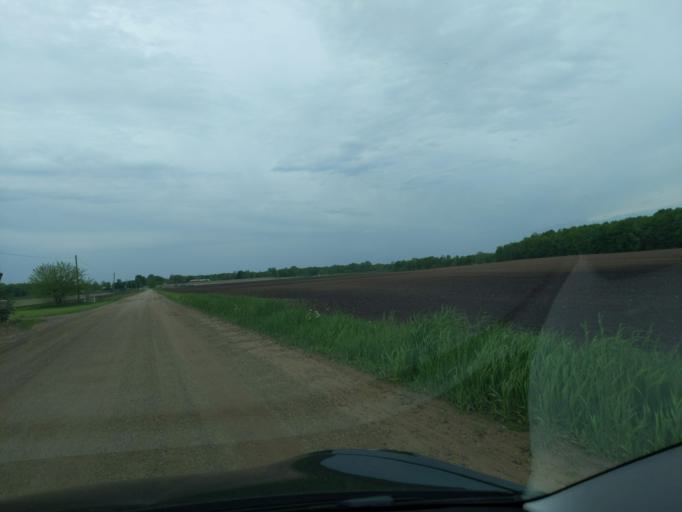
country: US
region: Michigan
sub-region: Ingham County
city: Stockbridge
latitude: 42.4206
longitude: -84.2141
